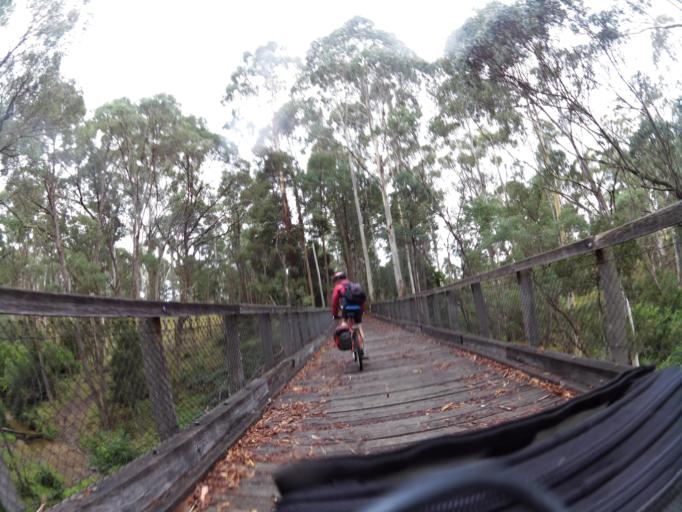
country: AU
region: New South Wales
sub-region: Greater Hume Shire
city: Holbrook
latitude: -36.1611
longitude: 147.4867
